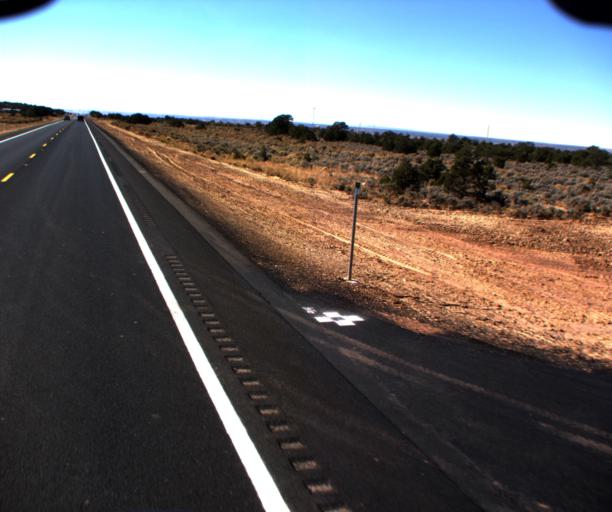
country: US
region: Arizona
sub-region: Apache County
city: Ganado
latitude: 35.7176
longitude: -109.4035
